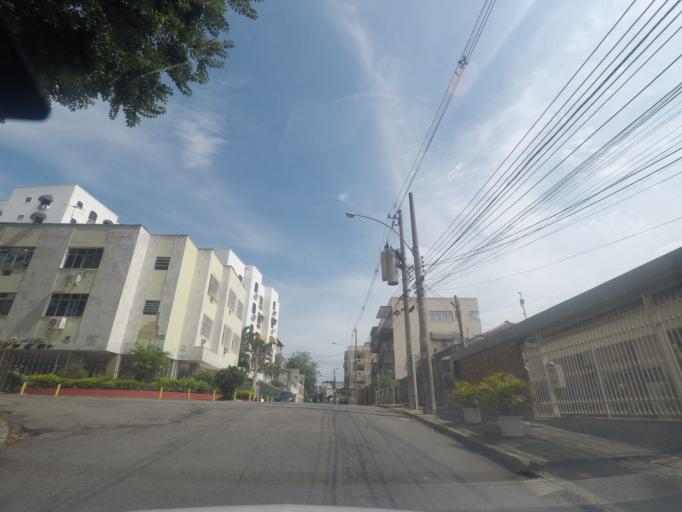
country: BR
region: Rio de Janeiro
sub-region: Rio De Janeiro
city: Rio de Janeiro
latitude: -22.8165
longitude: -43.1995
